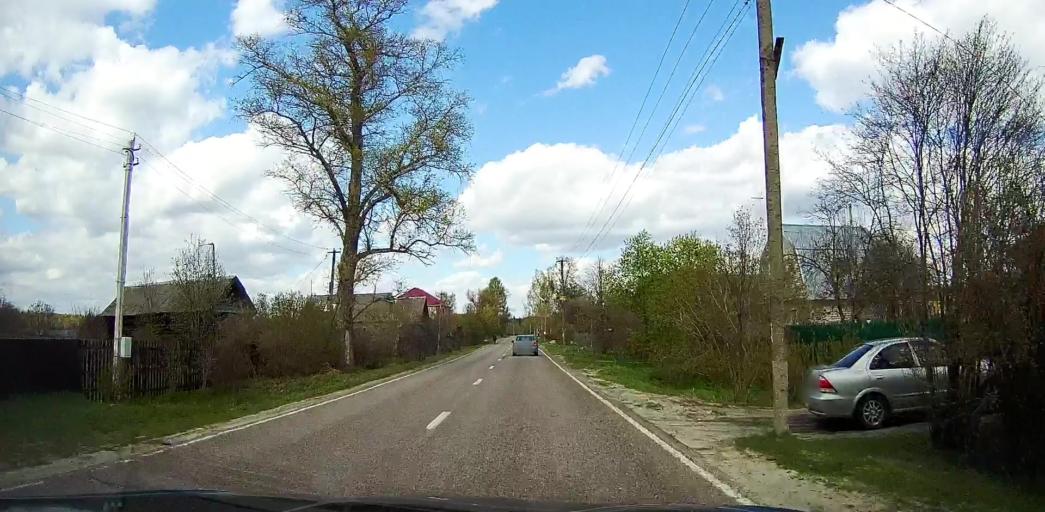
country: RU
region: Moskovskaya
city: Davydovo
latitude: 55.5844
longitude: 38.8275
